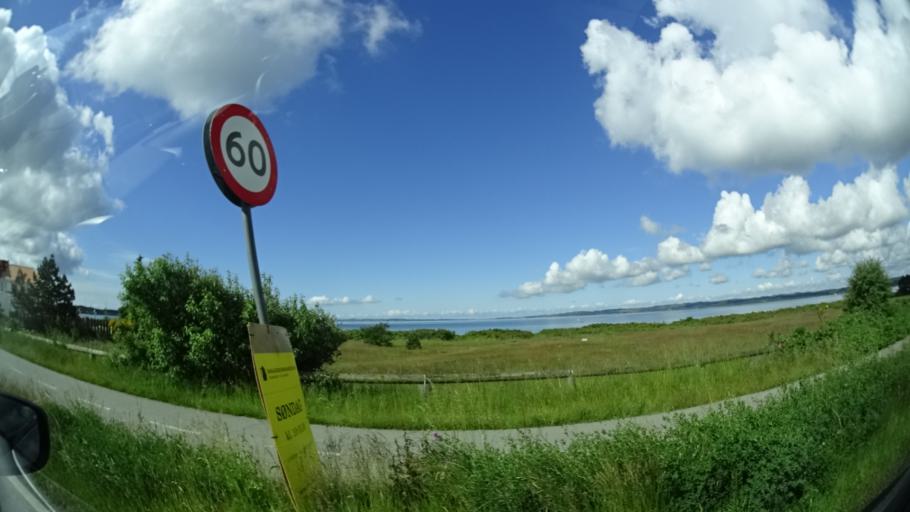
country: DK
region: Central Jutland
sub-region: Syddjurs Kommune
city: Ebeltoft
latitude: 56.2151
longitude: 10.6751
